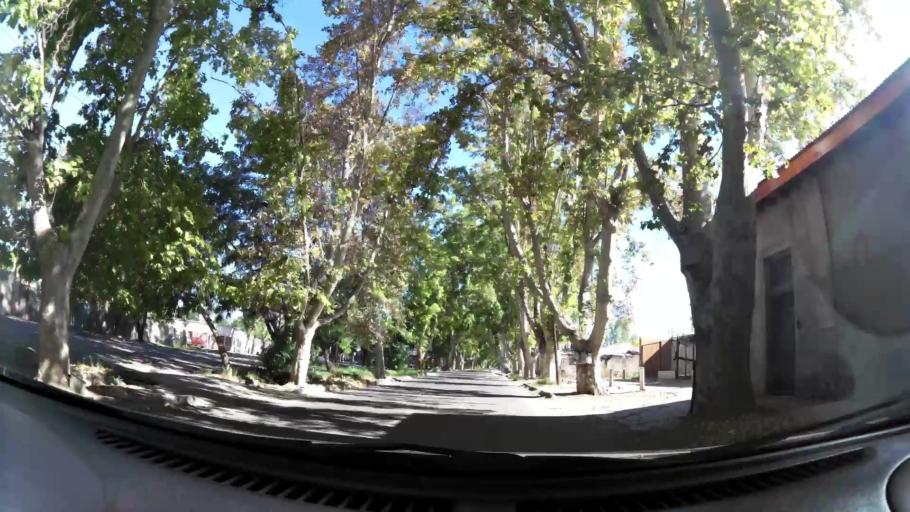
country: AR
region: Mendoza
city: Las Heras
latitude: -32.8382
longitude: -68.8252
